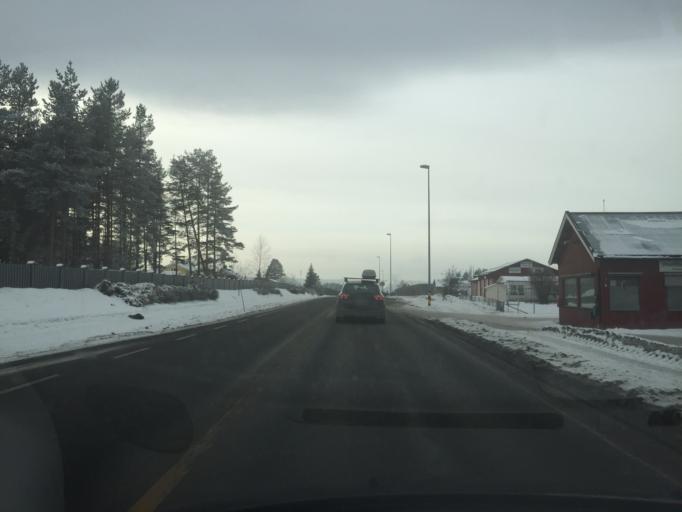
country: NO
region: Hedmark
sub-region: Elverum
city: Elverum
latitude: 60.8994
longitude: 11.5931
